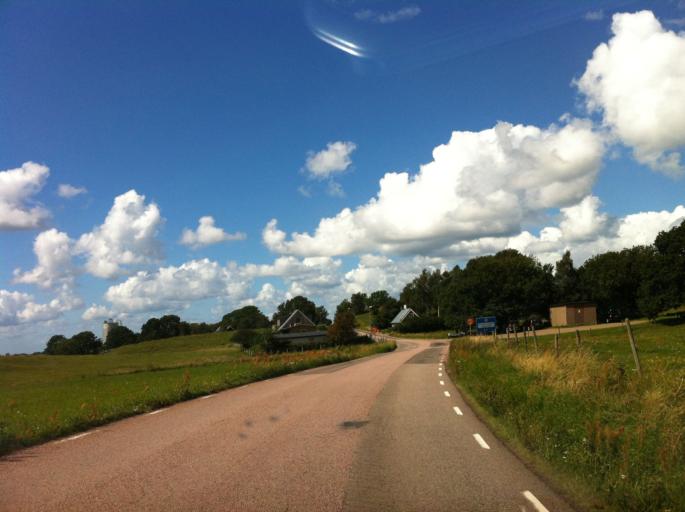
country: SE
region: Skane
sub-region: Angelholms Kommun
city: AEngelholm
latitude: 56.2431
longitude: 12.8703
